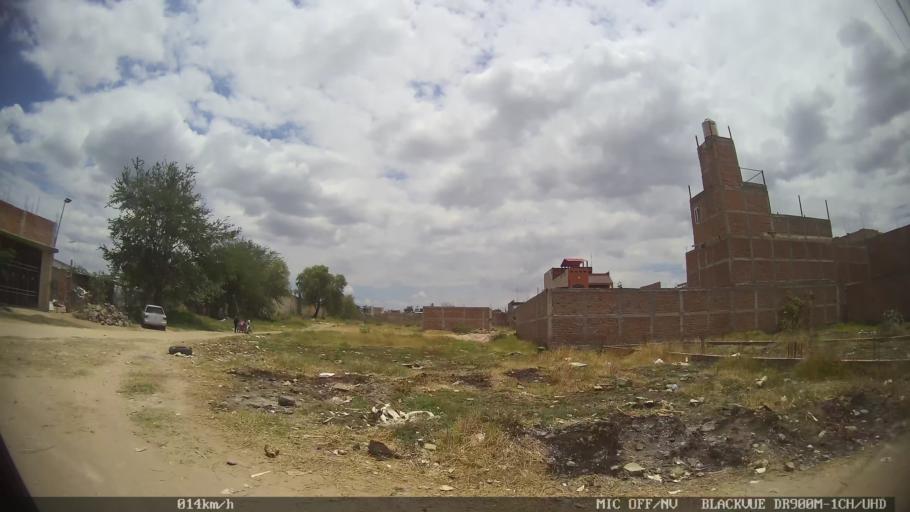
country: MX
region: Jalisco
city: Tlaquepaque
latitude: 20.6412
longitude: -103.2675
